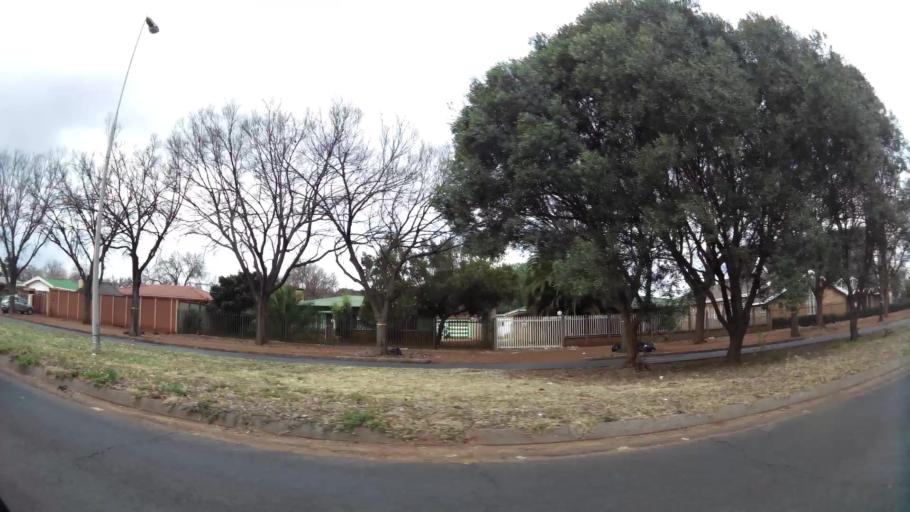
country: ZA
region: Gauteng
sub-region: Sedibeng District Municipality
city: Vanderbijlpark
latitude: -26.7043
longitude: 27.8238
